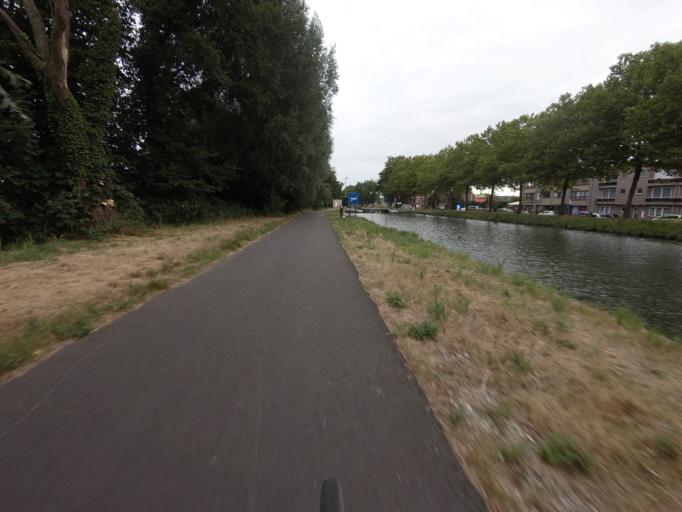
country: BE
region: Flanders
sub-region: Provincie Antwerpen
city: Schoten
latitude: 51.2511
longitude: 4.5069
